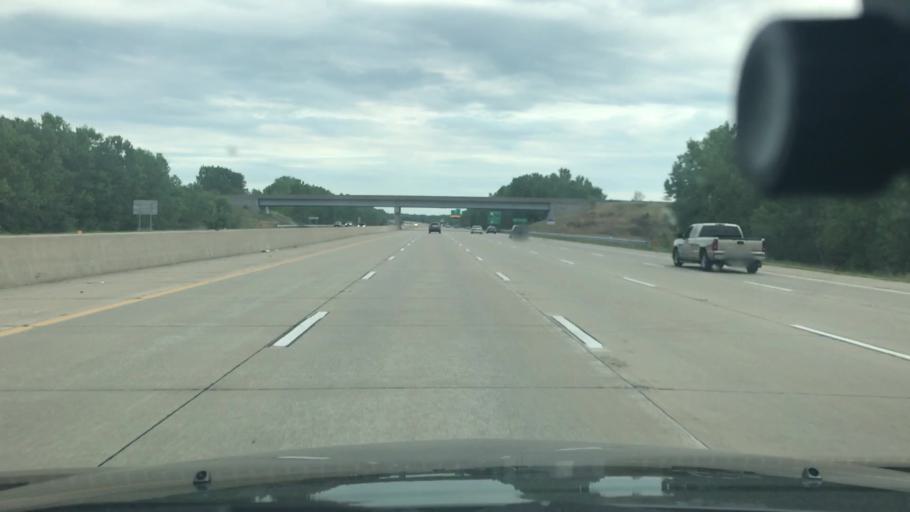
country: US
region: Missouri
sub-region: Saint Charles County
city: Saint Charles
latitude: 38.7209
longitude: -90.5116
